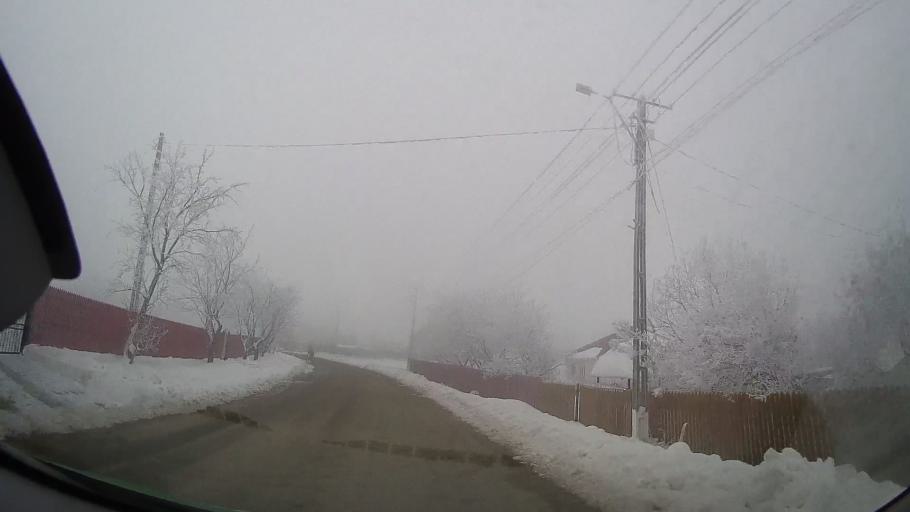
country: RO
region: Iasi
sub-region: Comuna Tansa
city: Suhulet
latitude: 46.9005
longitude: 27.2482
